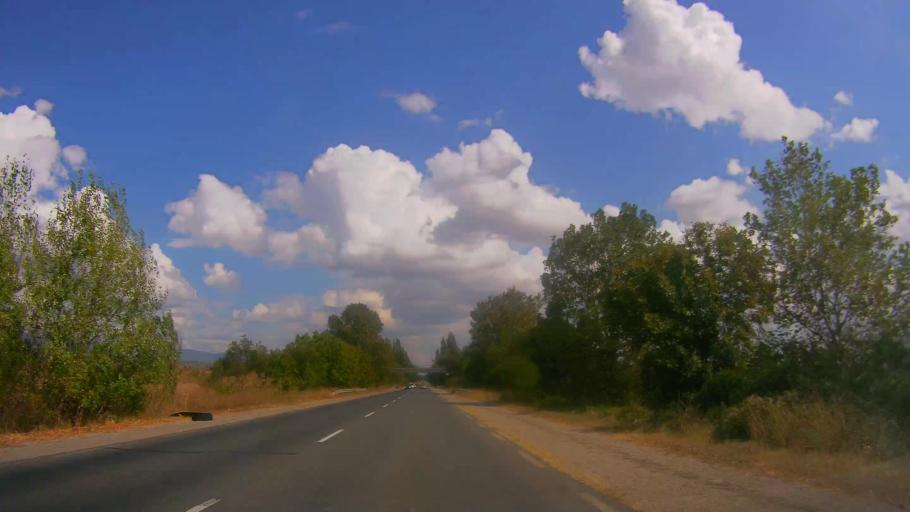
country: BG
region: Sliven
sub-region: Obshtina Sliven
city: Sliven
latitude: 42.6370
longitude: 26.2441
